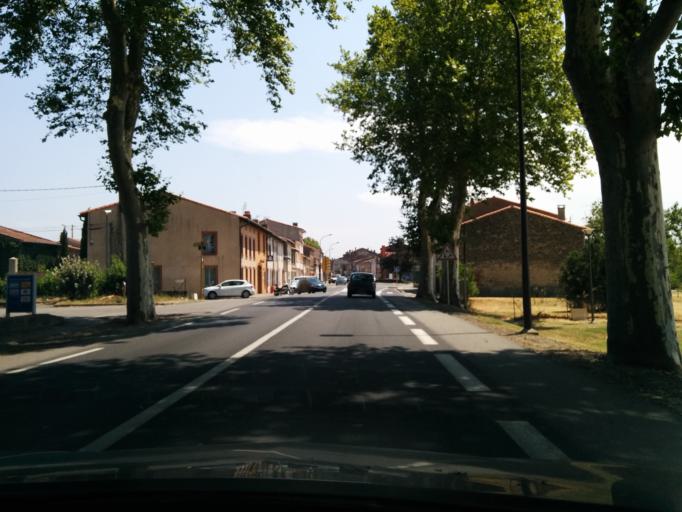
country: FR
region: Midi-Pyrenees
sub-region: Departement de la Haute-Garonne
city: Villefranche-de-Lauragais
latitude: 43.4028
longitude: 1.7122
